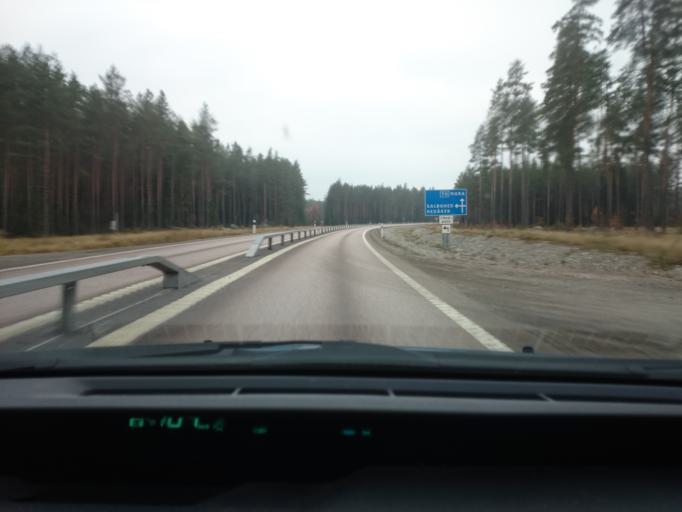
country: SE
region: Dalarna
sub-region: Avesta Kommun
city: Avesta
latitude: 60.0298
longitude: 16.3464
